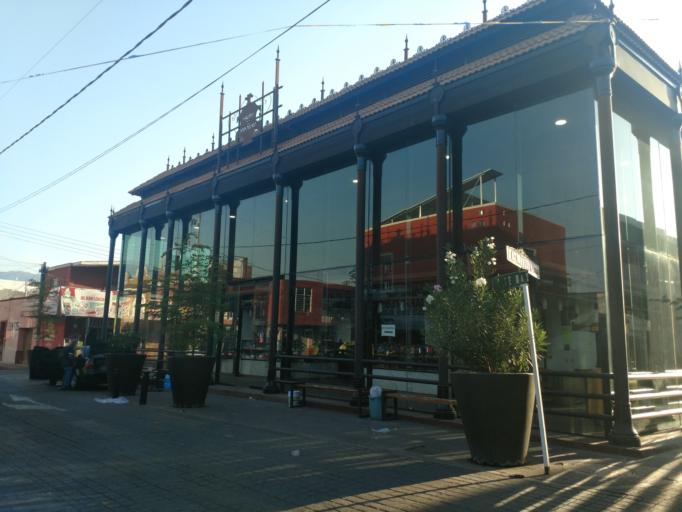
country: MX
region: Nayarit
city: Ixtlan del Rio
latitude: 21.0344
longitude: -104.3707
